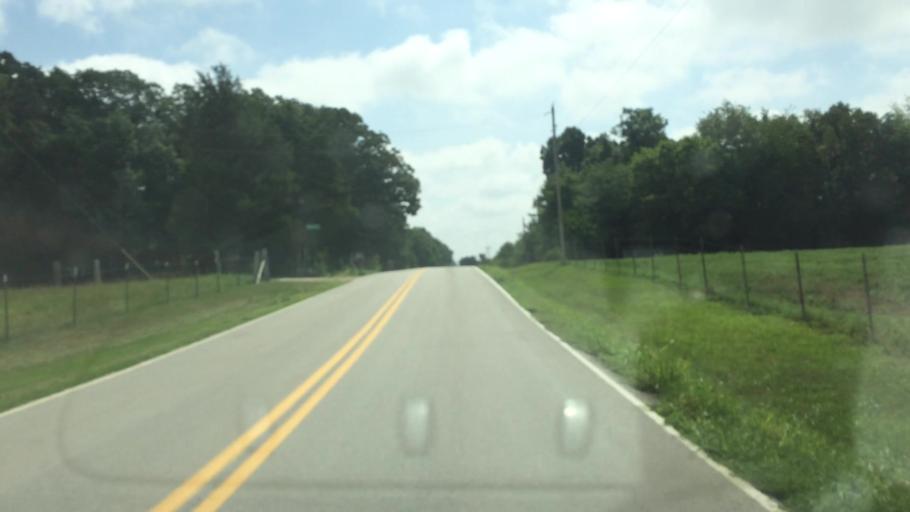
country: US
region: Missouri
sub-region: Greene County
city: Strafford
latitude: 37.2721
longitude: -93.1964
